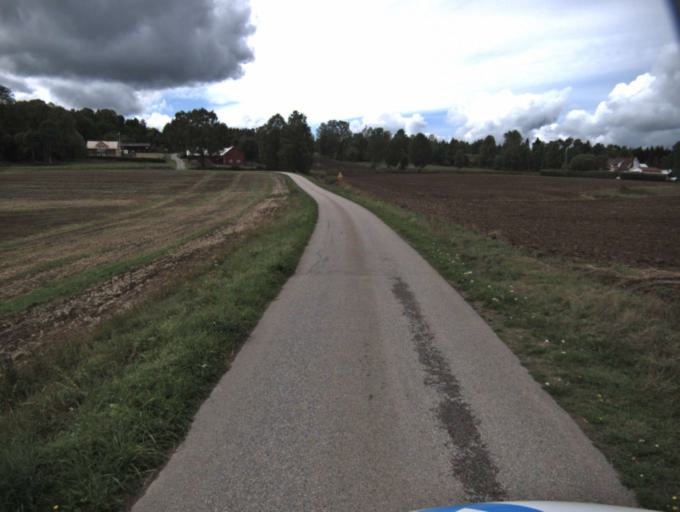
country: SE
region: Vaestra Goetaland
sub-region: Ulricehamns Kommun
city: Ulricehamn
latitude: 57.8554
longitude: 13.4254
